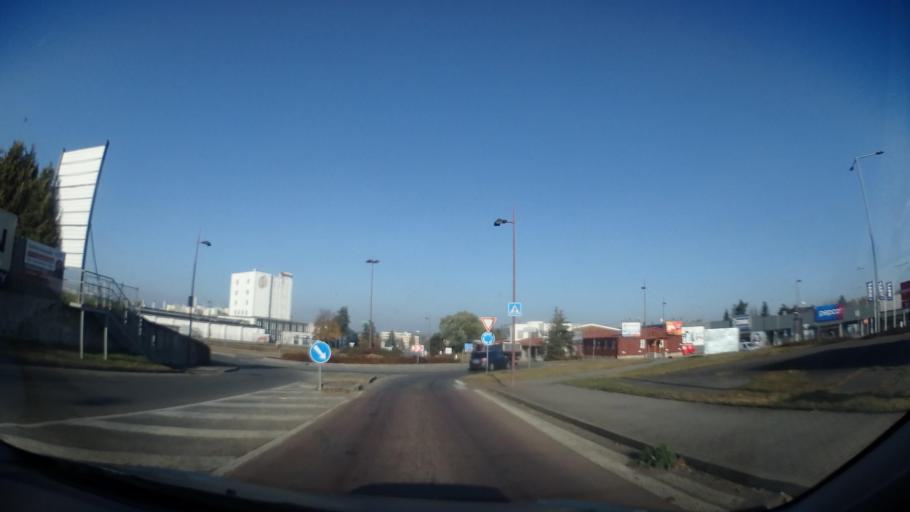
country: CZ
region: Vysocina
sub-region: Okres Zd'ar nad Sazavou
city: Zd'ar nad Sazavou
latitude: 49.5561
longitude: 15.9489
